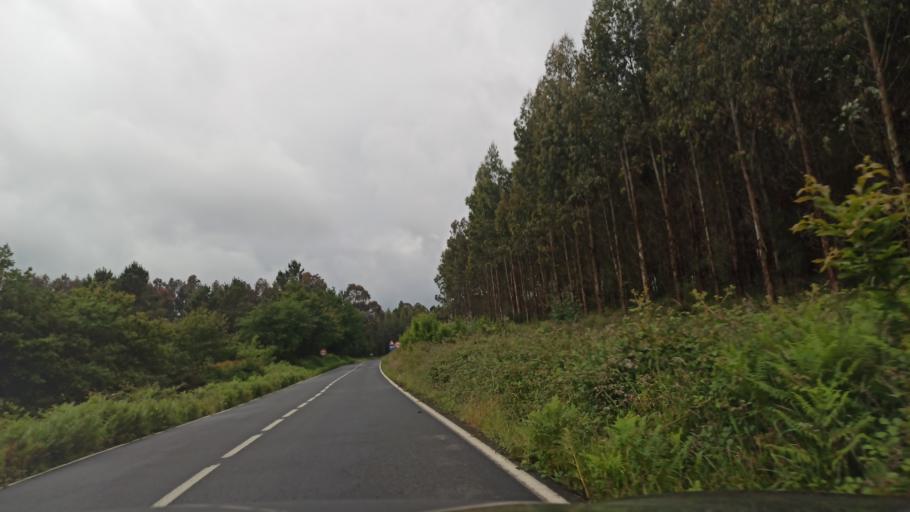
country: ES
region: Galicia
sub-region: Provincia da Coruna
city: Santiso
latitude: 42.7831
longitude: -8.0445
